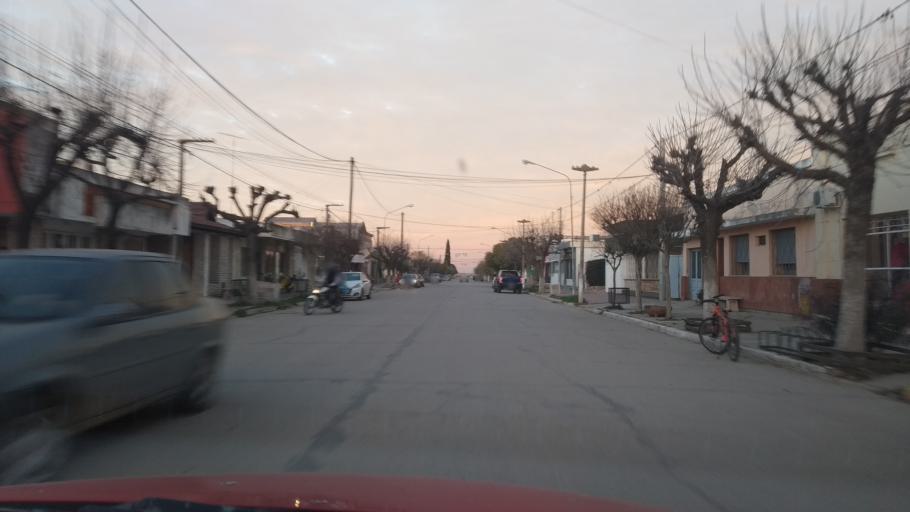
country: AR
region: Cordoba
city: Leones
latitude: -32.6302
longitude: -62.4795
